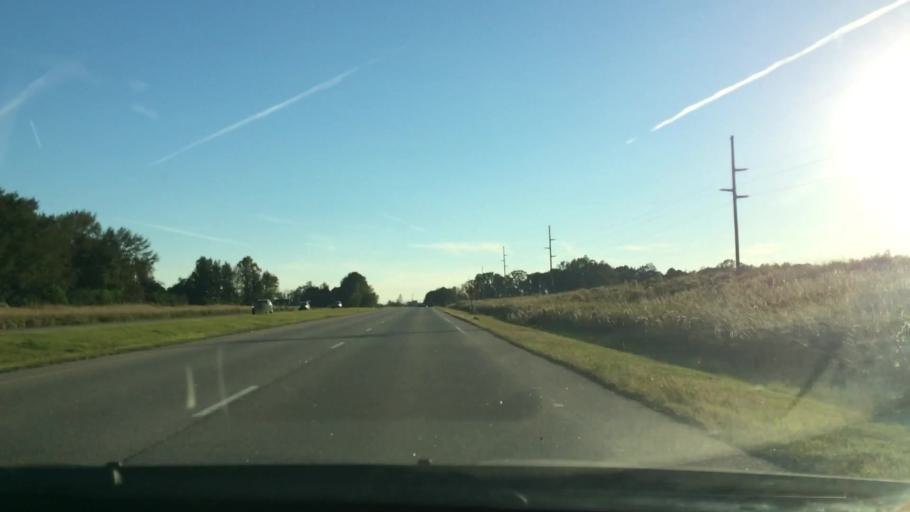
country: US
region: North Carolina
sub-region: Pitt County
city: Grifton
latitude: 35.3988
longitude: -77.4406
